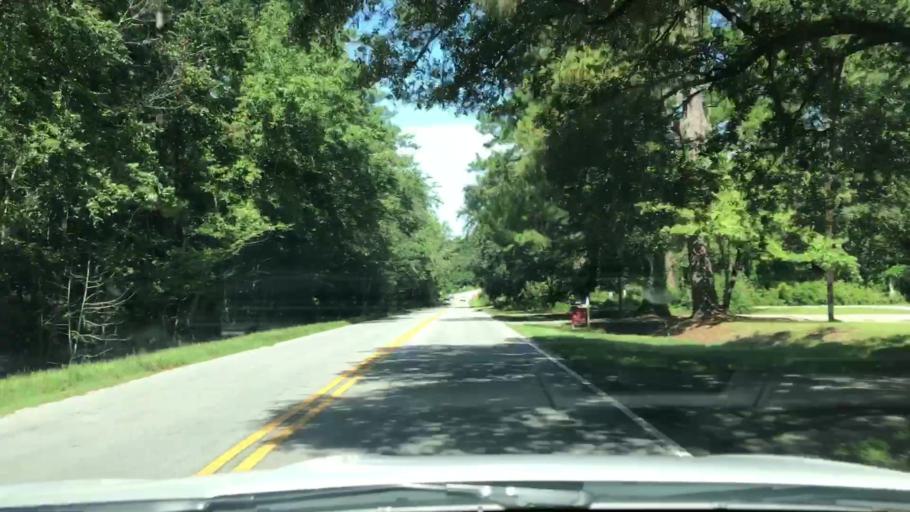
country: US
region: South Carolina
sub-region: Dorchester County
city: Centerville
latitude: 32.9458
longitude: -80.1975
